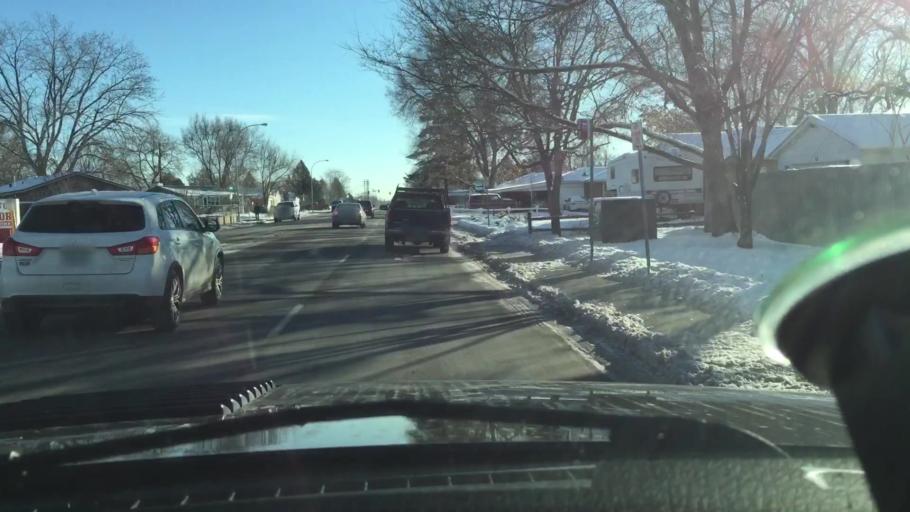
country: US
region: Colorado
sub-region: Adams County
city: Twin Lakes
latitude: 39.8272
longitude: -105.0203
